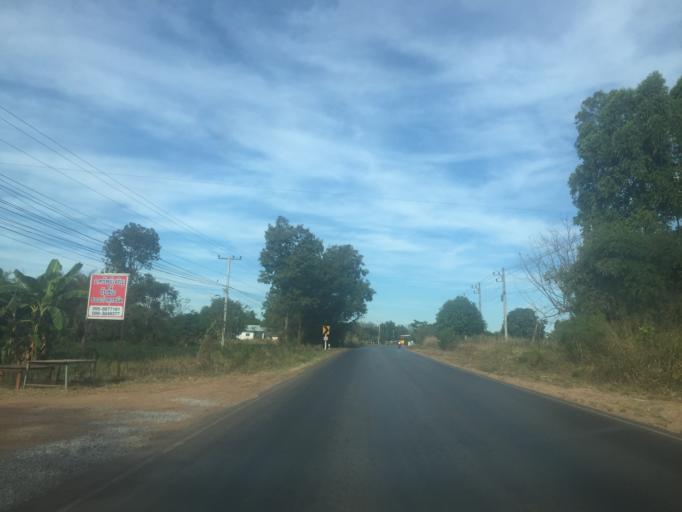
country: TH
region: Changwat Udon Thani
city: Si That
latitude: 16.9784
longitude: 103.1910
